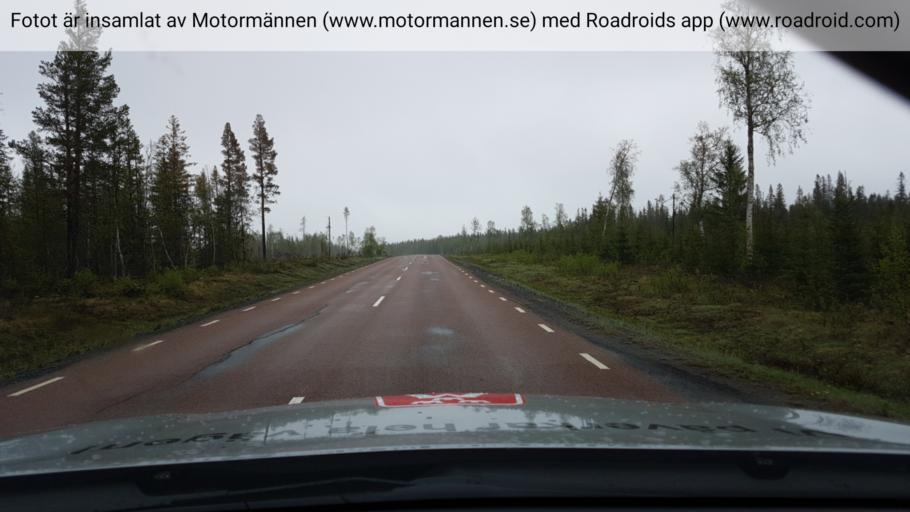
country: SE
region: Jaemtland
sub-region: Krokoms Kommun
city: Valla
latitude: 63.1335
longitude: 13.9382
